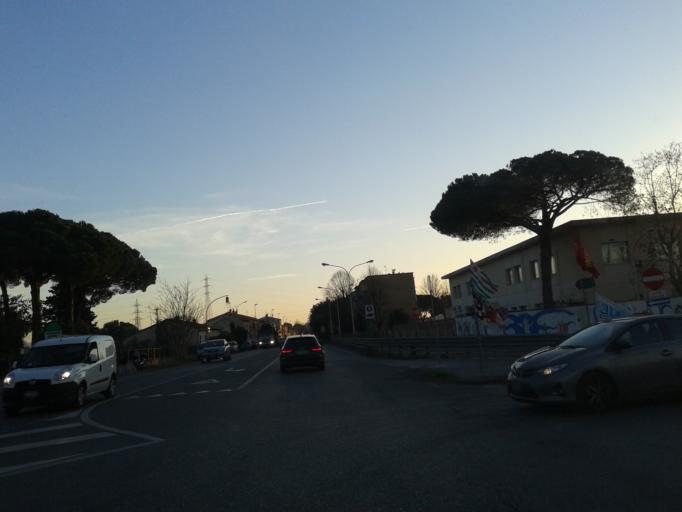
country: IT
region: Tuscany
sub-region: Provincia di Livorno
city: Livorno
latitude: 43.5829
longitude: 10.3441
